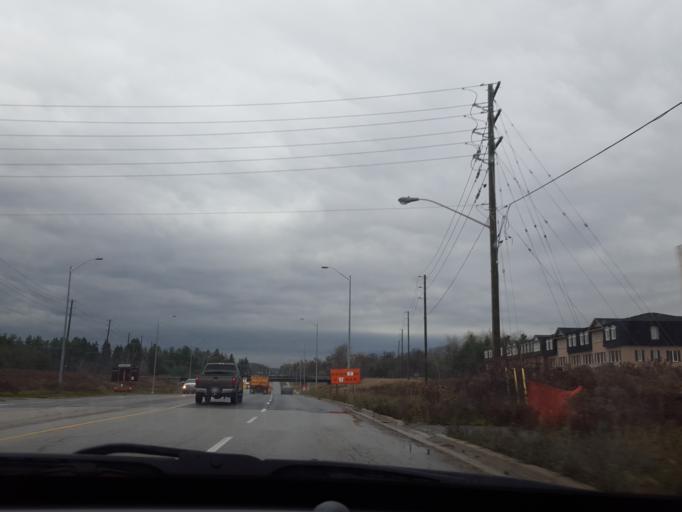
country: CA
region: Ontario
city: Pickering
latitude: 43.8806
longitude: -79.0882
